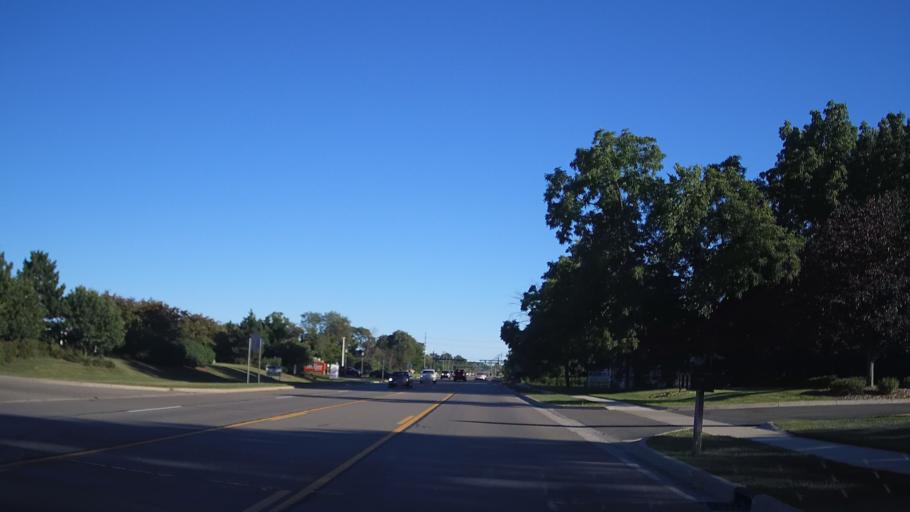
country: US
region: Michigan
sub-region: Macomb County
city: Shelby
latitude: 42.7168
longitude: -83.0355
